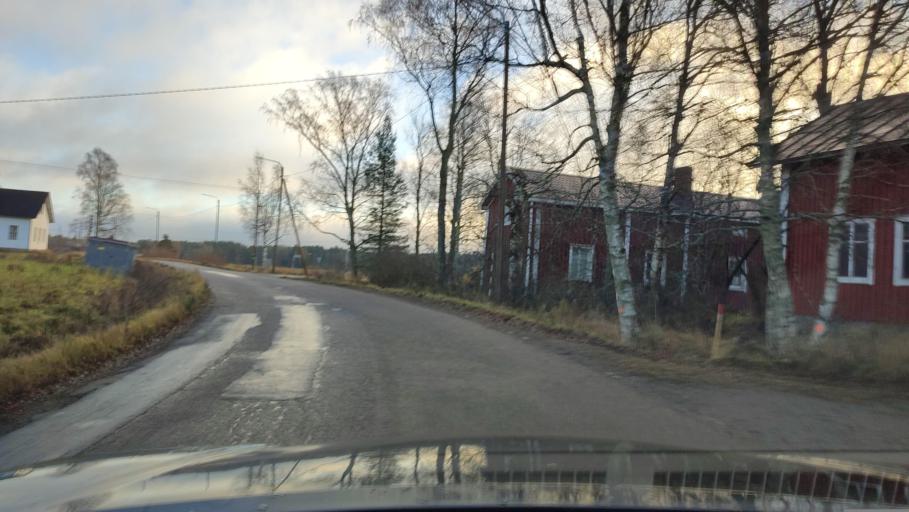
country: FI
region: Ostrobothnia
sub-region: Sydosterbotten
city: Naerpes
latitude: 62.4411
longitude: 21.3632
